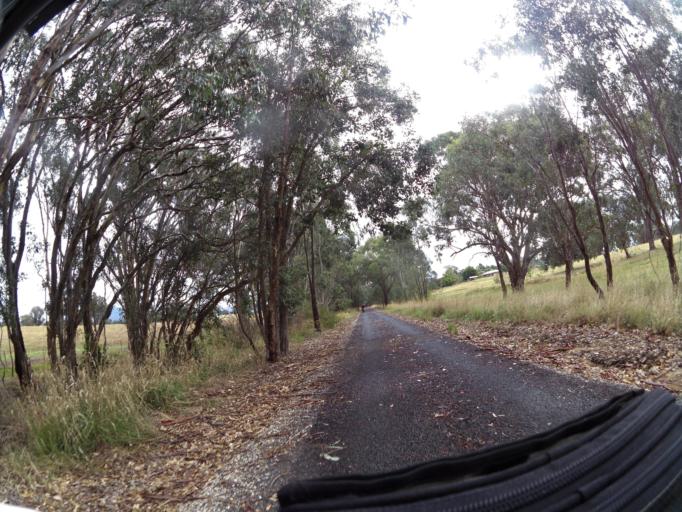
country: AU
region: New South Wales
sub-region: Albury Municipality
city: East Albury
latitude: -36.1434
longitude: 147.0039
